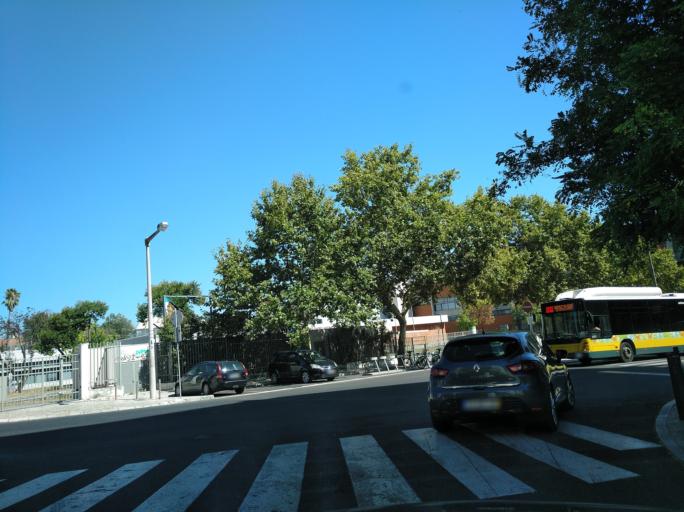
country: PT
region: Lisbon
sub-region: Loures
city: Moscavide
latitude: 38.7581
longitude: -9.1365
